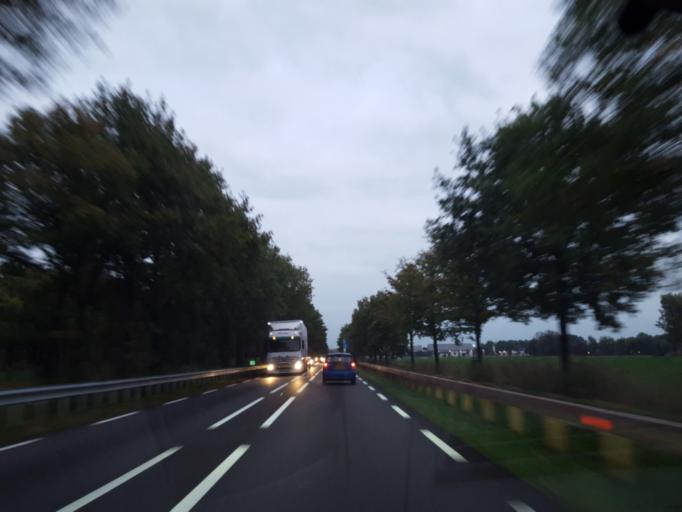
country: NL
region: North Brabant
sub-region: Gemeente Someren
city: Someren
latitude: 51.4037
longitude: 5.7139
